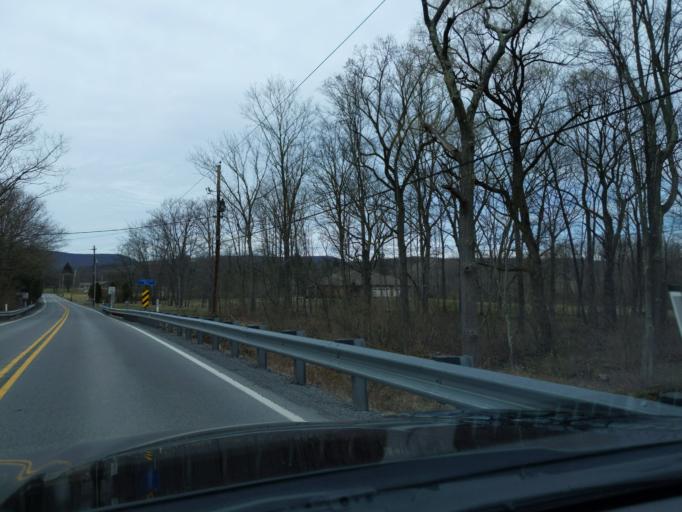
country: US
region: Pennsylvania
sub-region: Blair County
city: Greenwood
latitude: 40.5576
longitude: -78.3770
